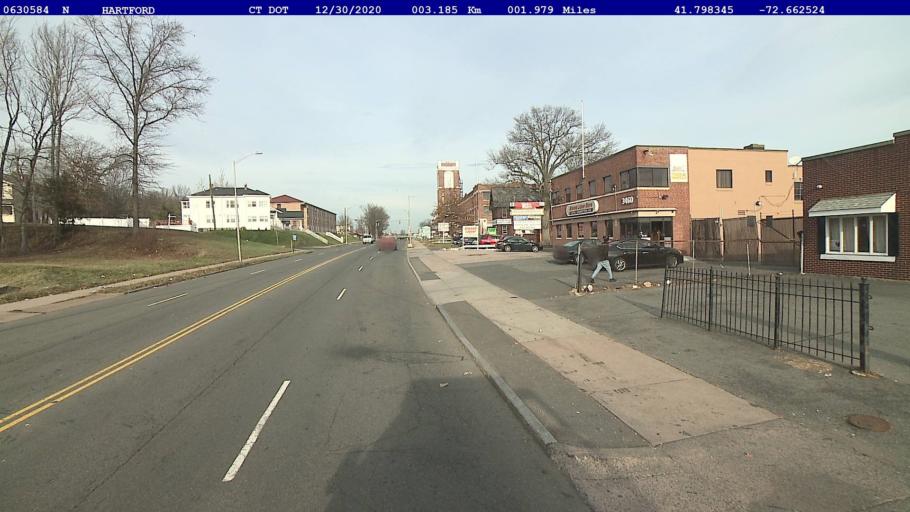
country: US
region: Connecticut
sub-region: Hartford County
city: Blue Hills
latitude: 41.7984
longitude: -72.6625
